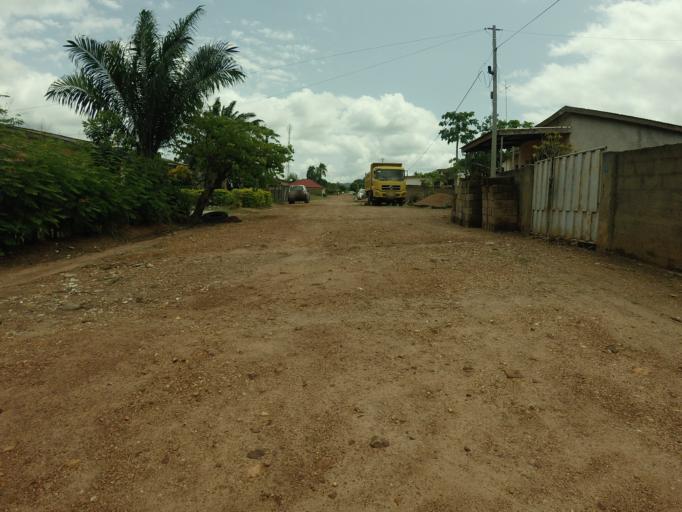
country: GH
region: Volta
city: Ho
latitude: 6.5895
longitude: 0.4771
